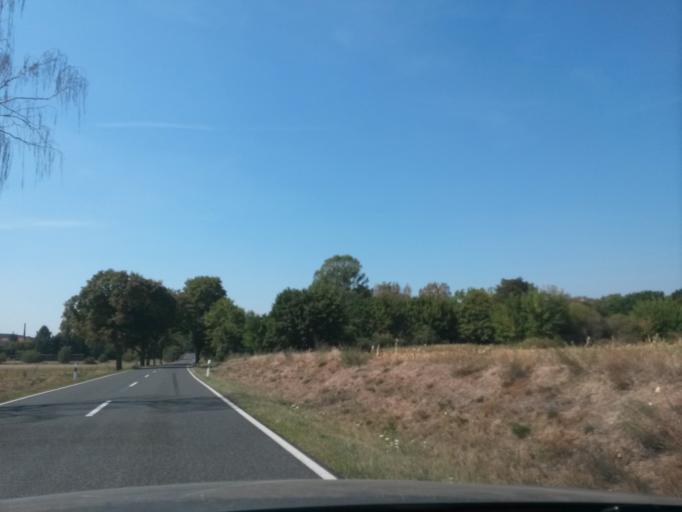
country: DE
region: Brandenburg
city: Gorzke
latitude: 52.1731
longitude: 12.3839
